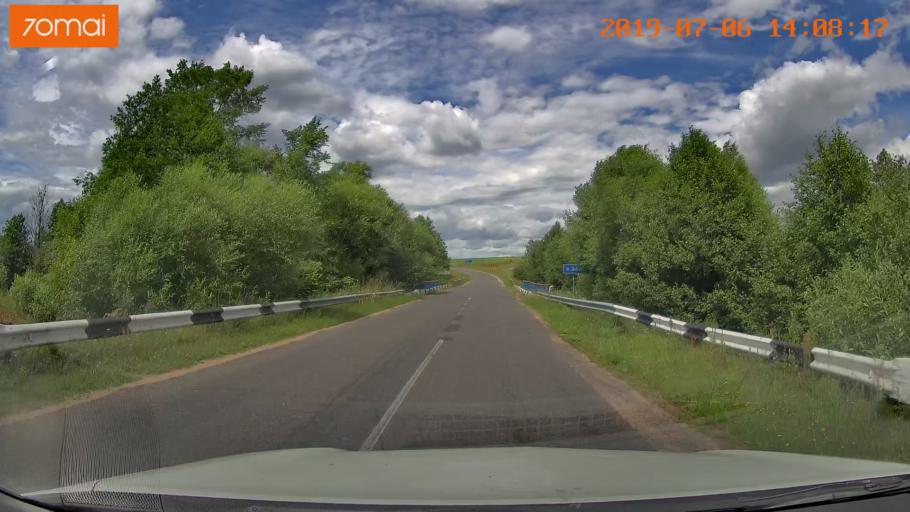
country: BY
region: Minsk
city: Ivyanyets
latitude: 53.8737
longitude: 26.7590
